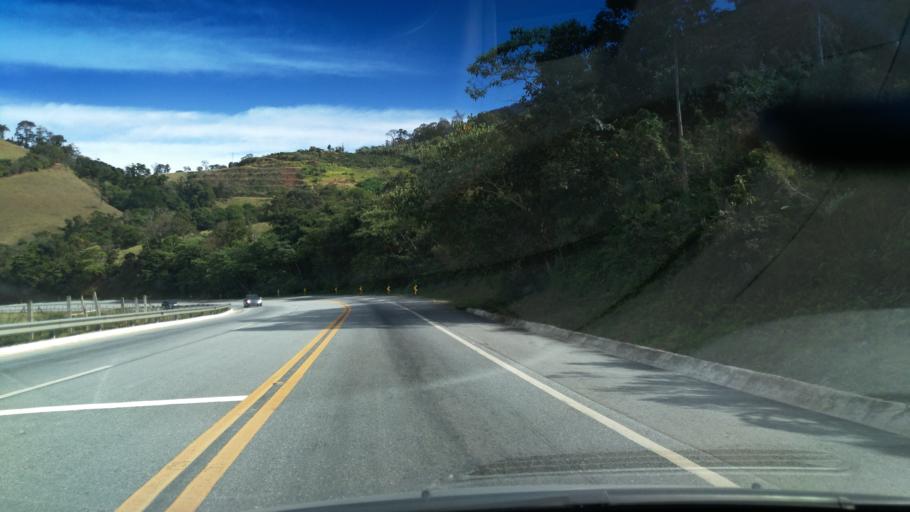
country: BR
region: Minas Gerais
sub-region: Borda Da Mata
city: Borda da Mata
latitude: -22.1308
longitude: -46.1476
